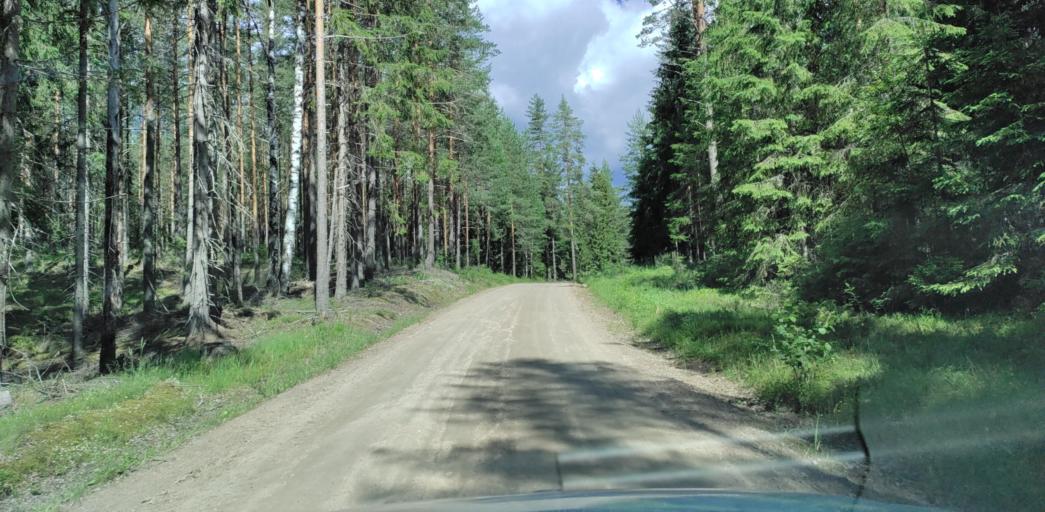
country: SE
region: Vaermland
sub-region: Sunne Kommun
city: Sunne
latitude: 60.0516
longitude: 13.2620
